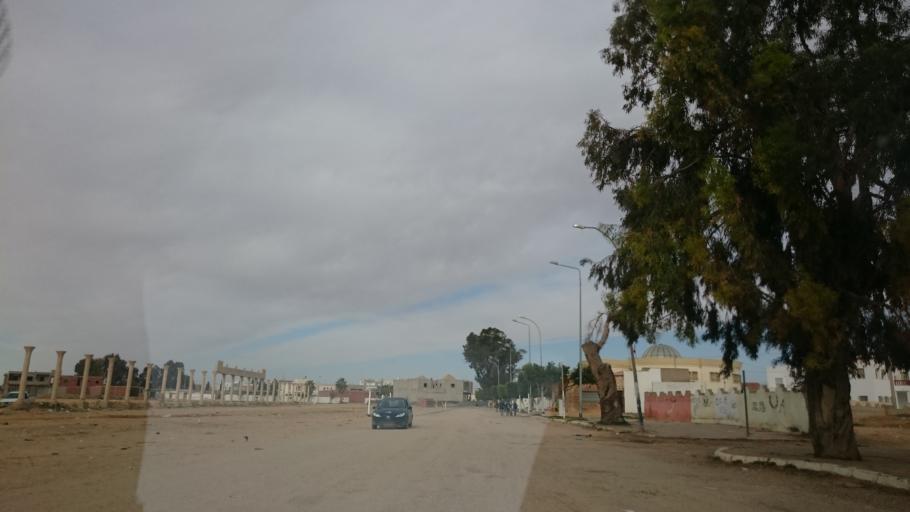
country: TN
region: Safaqis
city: Sfax
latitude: 34.7401
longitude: 10.5337
